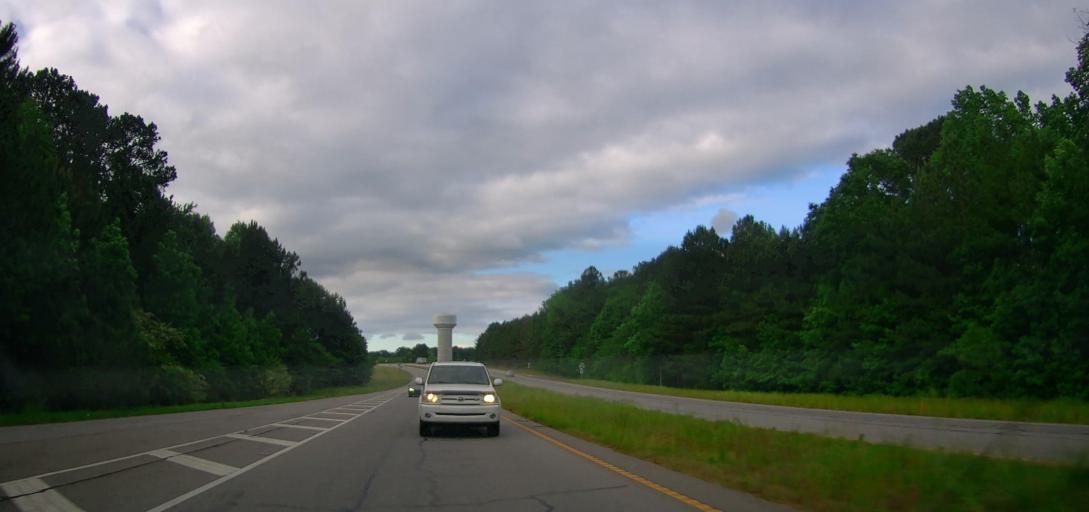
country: US
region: Georgia
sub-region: Oconee County
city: Watkinsville
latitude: 33.8427
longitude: -83.4250
